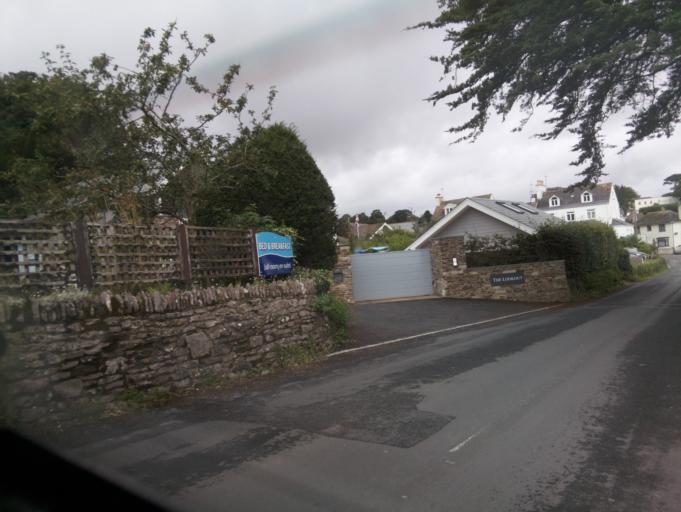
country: GB
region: England
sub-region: Devon
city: Dartmouth
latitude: 50.3231
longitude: -3.5984
